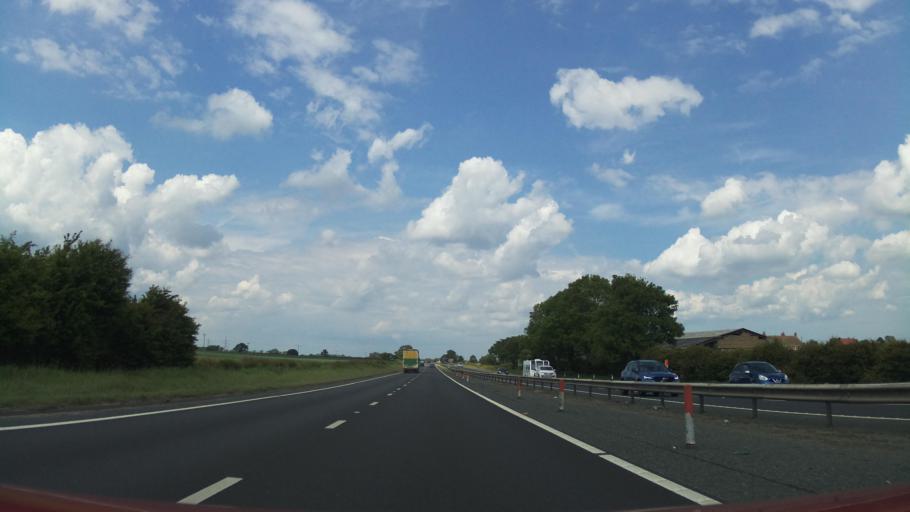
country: GB
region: England
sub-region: Stockton-on-Tees
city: Yarm
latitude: 54.4068
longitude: -1.3197
